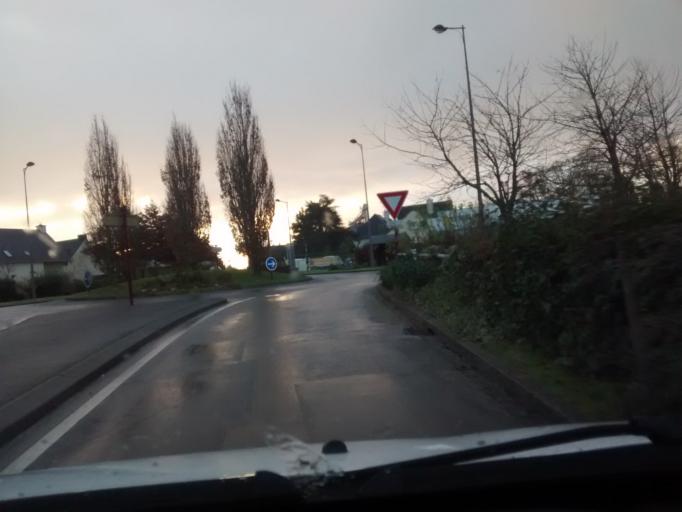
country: FR
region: Brittany
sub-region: Departement d'Ille-et-Vilaine
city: Bais
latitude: 48.0150
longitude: -1.2978
